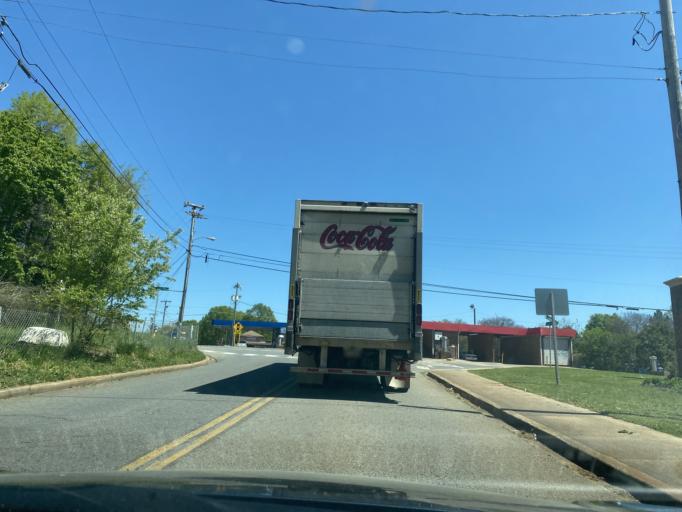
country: US
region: South Carolina
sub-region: Cherokee County
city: Gaffney
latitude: 35.0577
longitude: -81.6423
